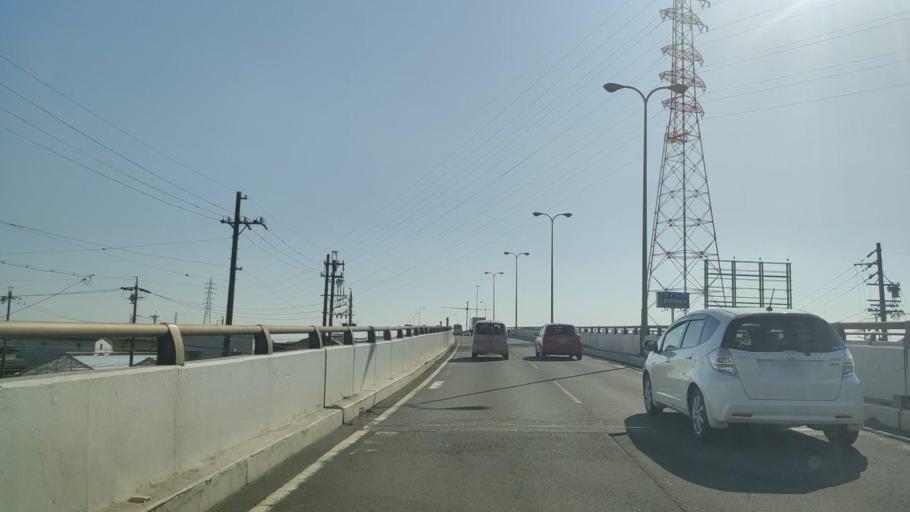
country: JP
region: Gifu
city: Gifu-shi
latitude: 35.4219
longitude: 136.7286
